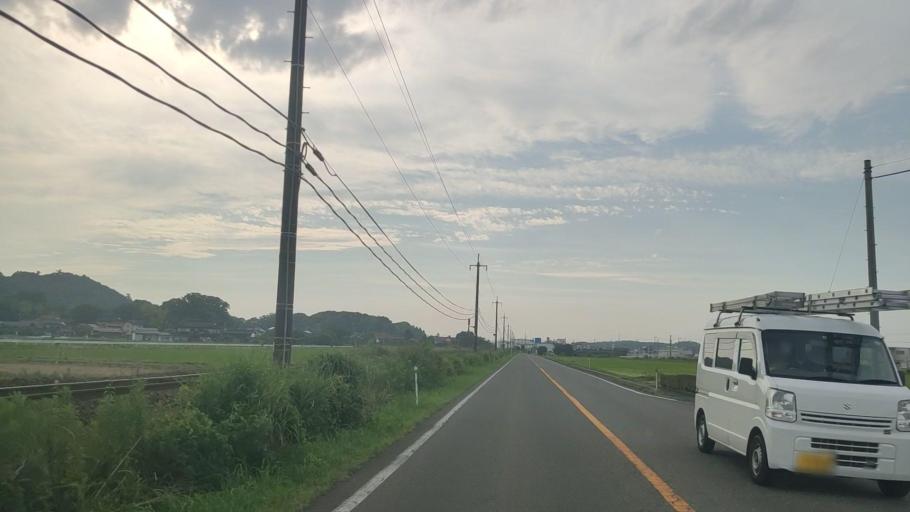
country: JP
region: Tottori
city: Kurayoshi
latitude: 35.4776
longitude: 133.8182
